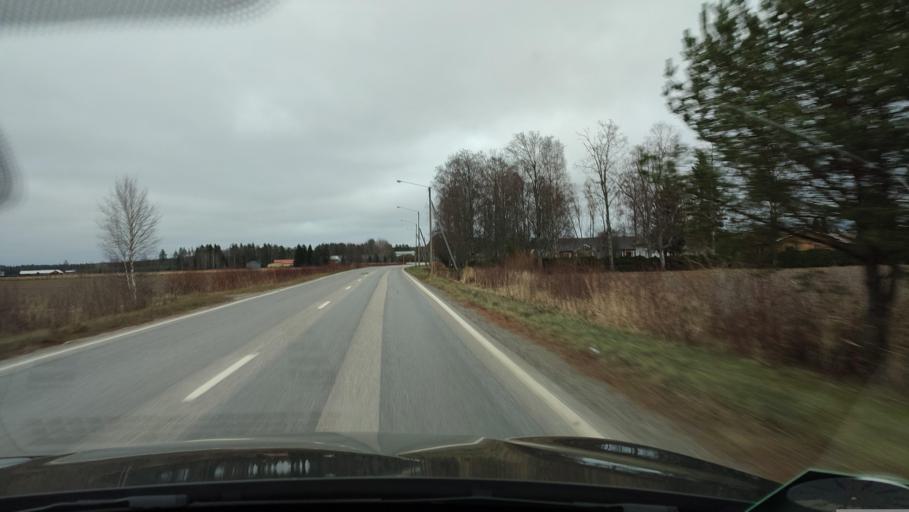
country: FI
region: Southern Ostrobothnia
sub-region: Suupohja
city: Karijoki
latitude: 62.2355
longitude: 21.6709
